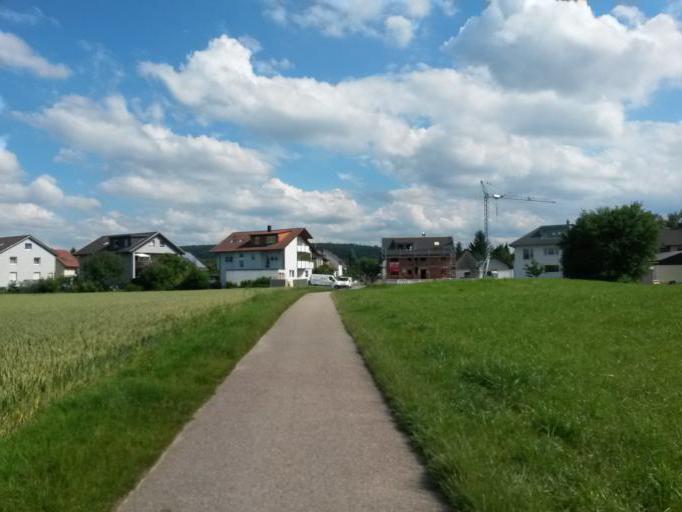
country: DE
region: Baden-Wuerttemberg
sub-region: Karlsruhe Region
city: Konigsbach-Stein
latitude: 48.9491
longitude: 8.5693
